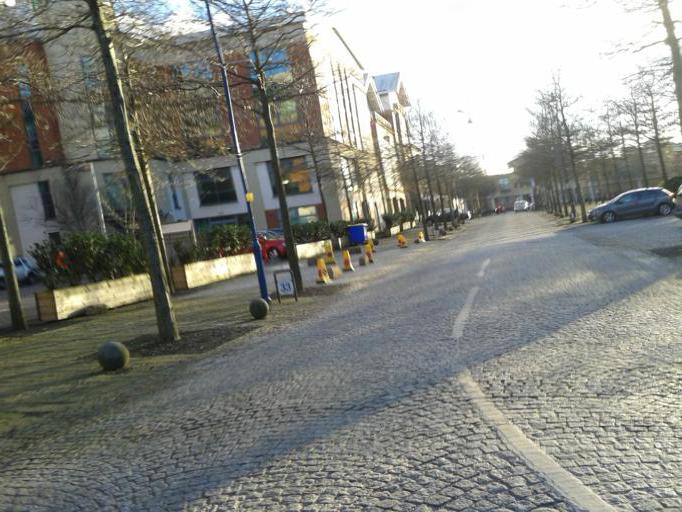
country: GB
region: Northern Ireland
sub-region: City of Belfast
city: Belfast
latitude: 54.6078
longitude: -5.9167
